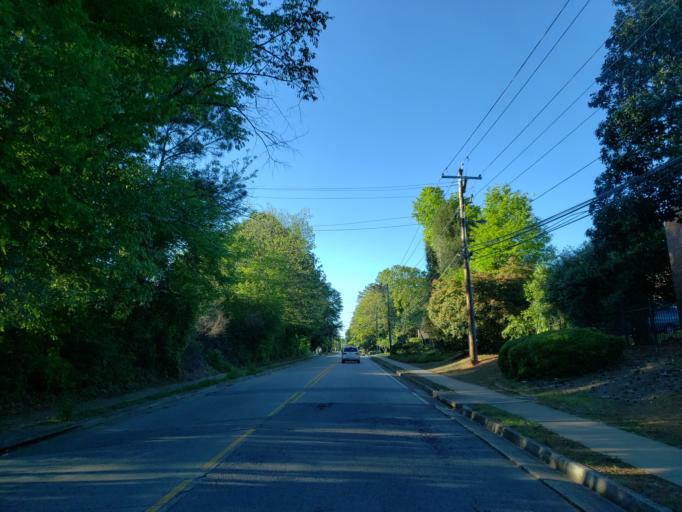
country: US
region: Georgia
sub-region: Cobb County
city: Fair Oaks
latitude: 33.9039
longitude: -84.5400
